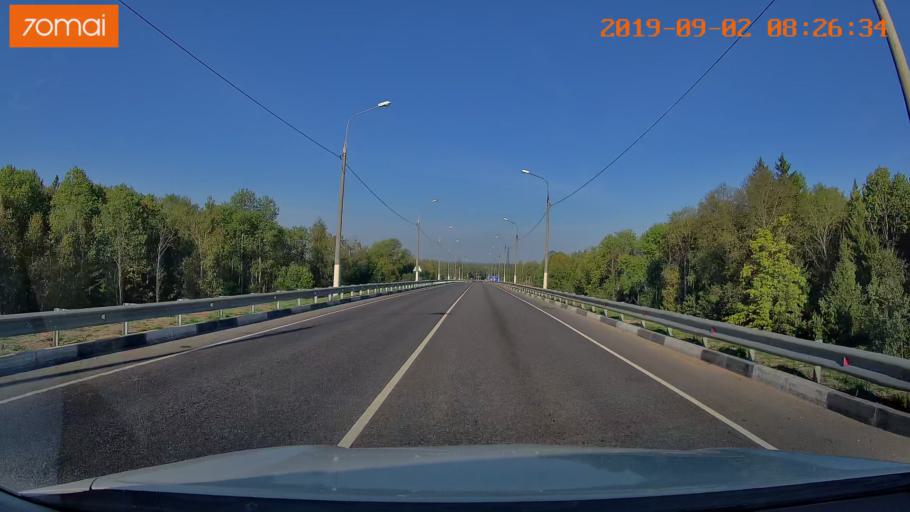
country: RU
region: Kaluga
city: Maloyaroslavets
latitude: 54.9791
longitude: 36.4326
